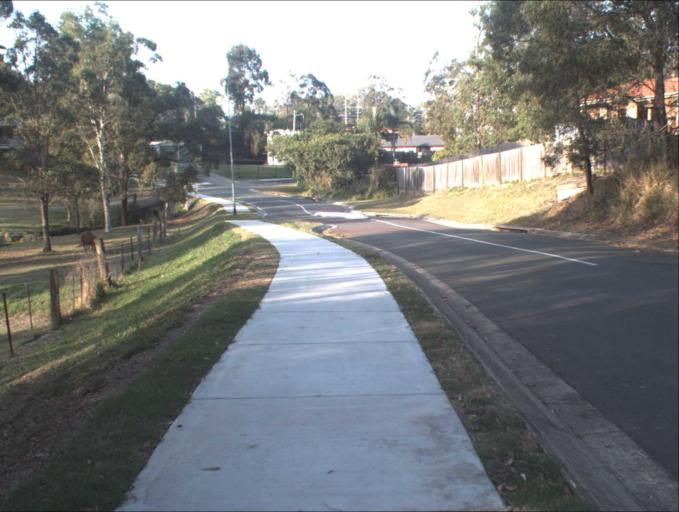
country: AU
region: Queensland
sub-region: Logan
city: Beenleigh
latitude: -27.6721
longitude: 153.2005
